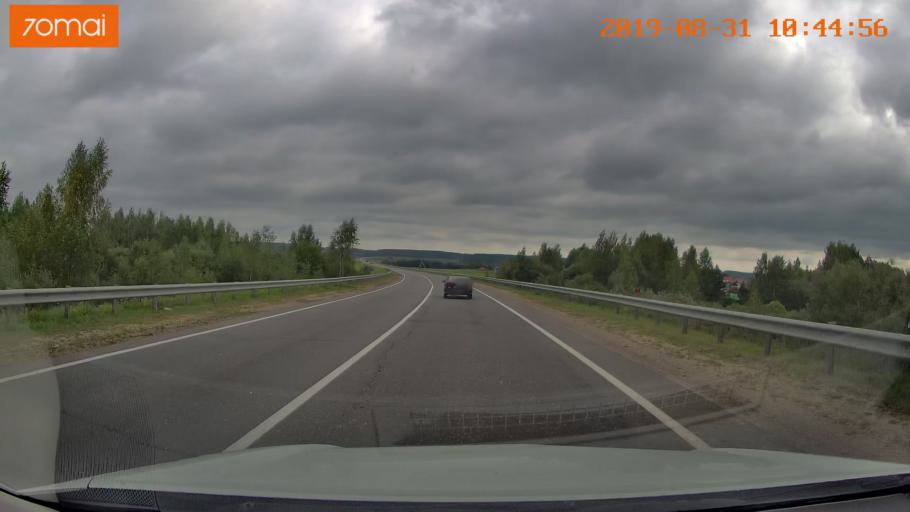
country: BY
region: Mogilev
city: Palykavichy Pyershyya
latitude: 53.9713
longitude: 30.3695
